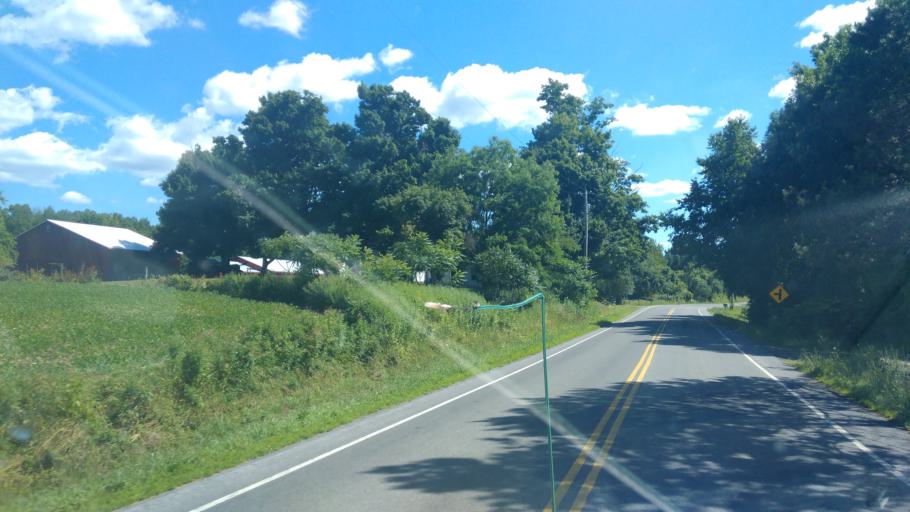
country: US
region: New York
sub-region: Wayne County
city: Sodus
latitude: 43.1593
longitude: -77.0121
